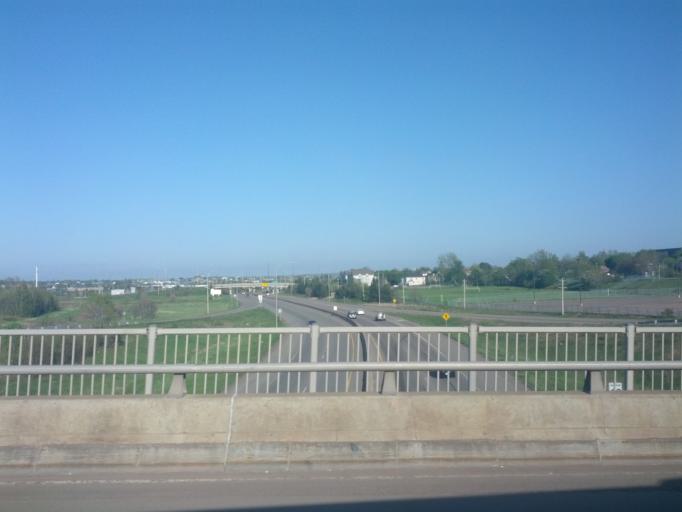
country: CA
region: New Brunswick
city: Moncton
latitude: 46.1003
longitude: -64.7858
